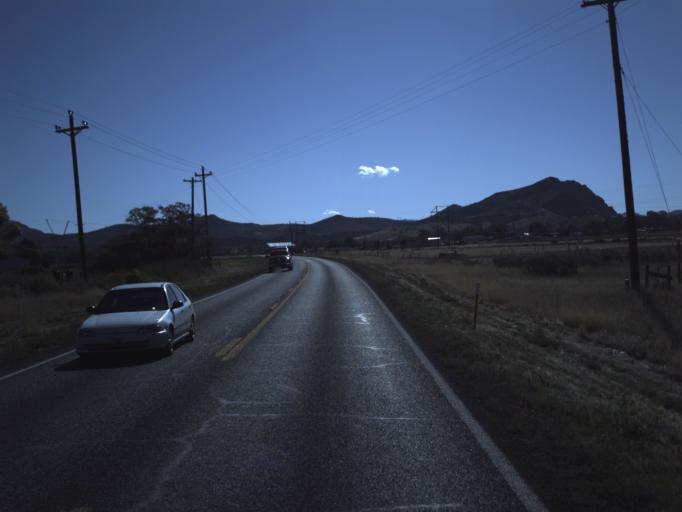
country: US
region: Utah
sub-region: Washington County
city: Enterprise
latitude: 37.6737
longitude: -113.5569
